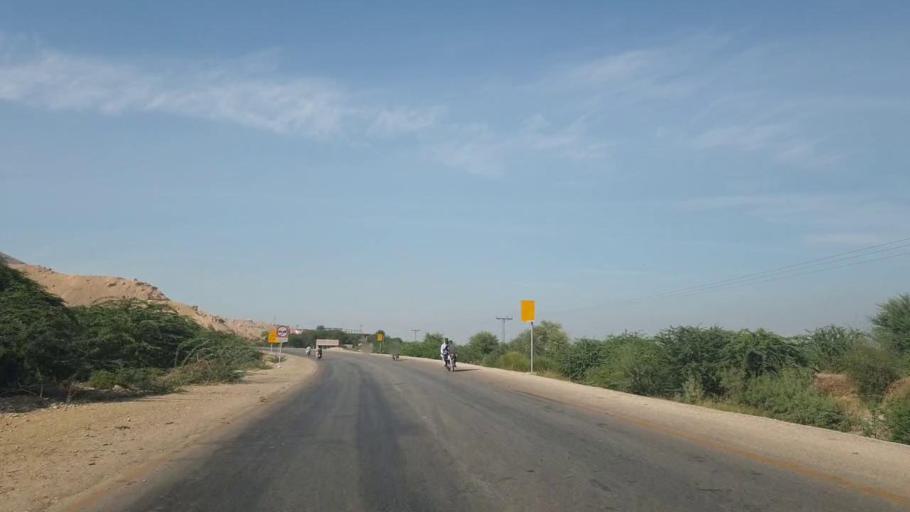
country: PK
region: Sindh
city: Sehwan
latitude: 26.3136
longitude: 67.8914
